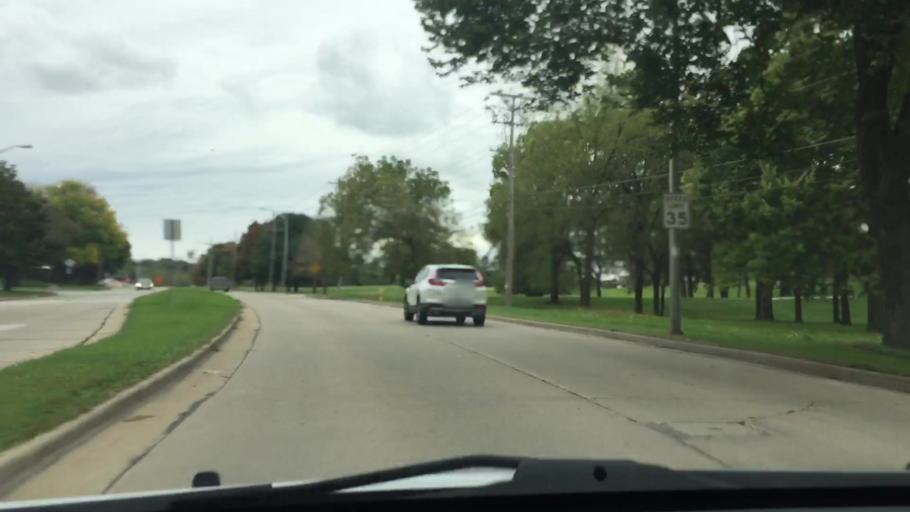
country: US
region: Wisconsin
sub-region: Waukesha County
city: Waukesha
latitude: 43.0322
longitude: -88.2457
